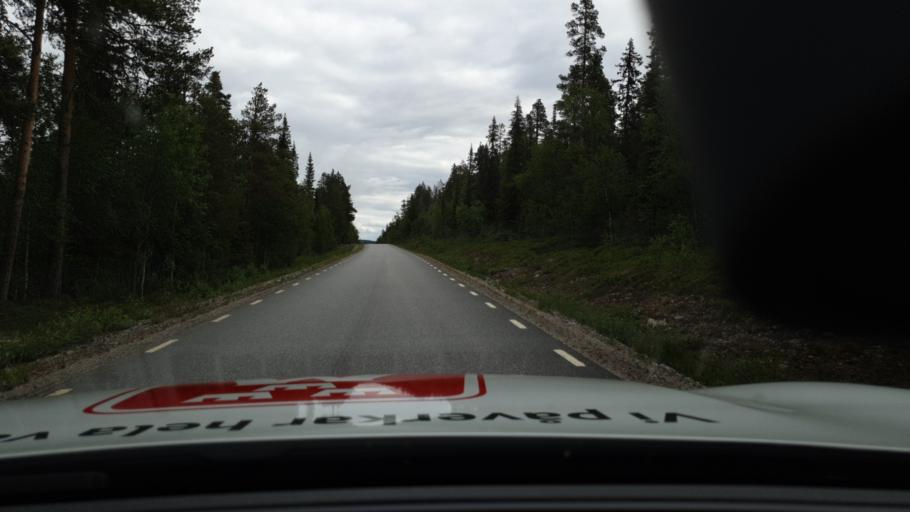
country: SE
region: Norrbotten
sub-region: Arjeplogs Kommun
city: Arjeplog
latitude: 66.8944
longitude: 17.9427
